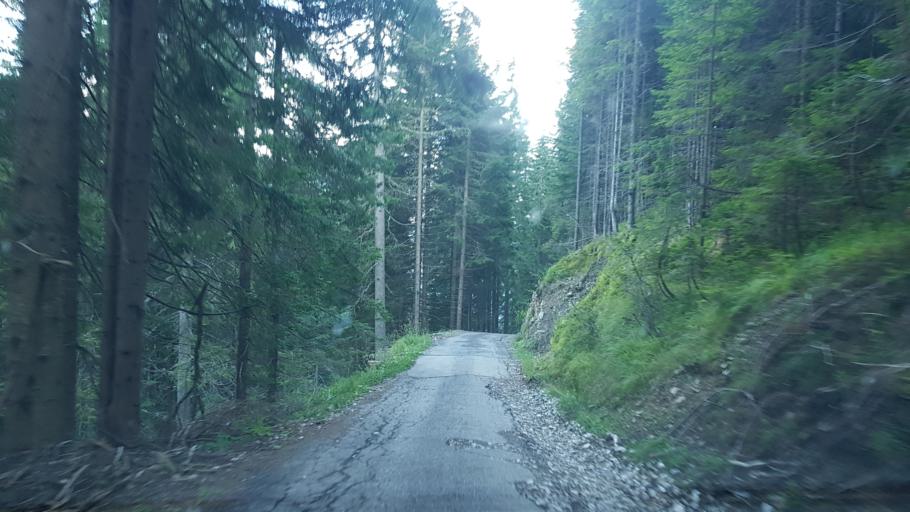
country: IT
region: Veneto
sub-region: Provincia di Belluno
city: San Pietro di Cadore
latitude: 46.5971
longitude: 12.5917
